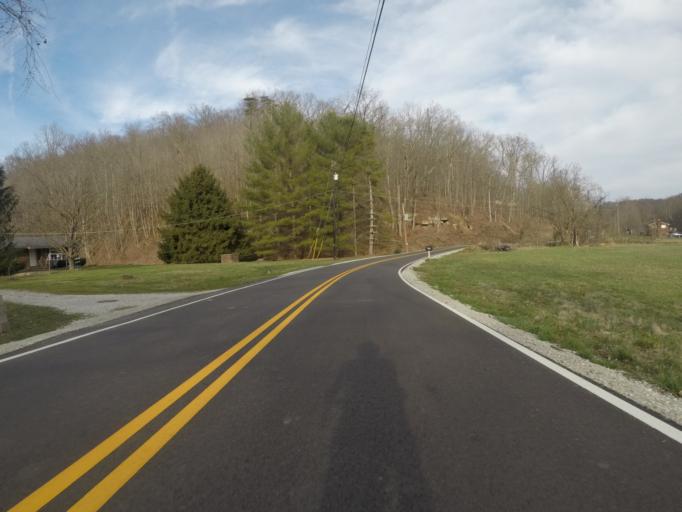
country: US
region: Ohio
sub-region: Lawrence County
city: Burlington
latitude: 38.4786
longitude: -82.5111
